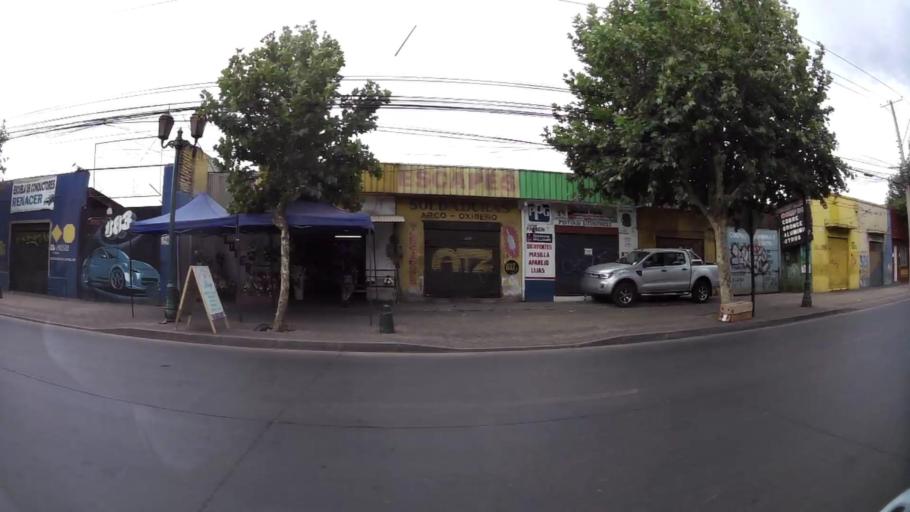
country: CL
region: O'Higgins
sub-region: Provincia de Cachapoal
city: Rancagua
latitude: -34.1644
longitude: -70.7462
